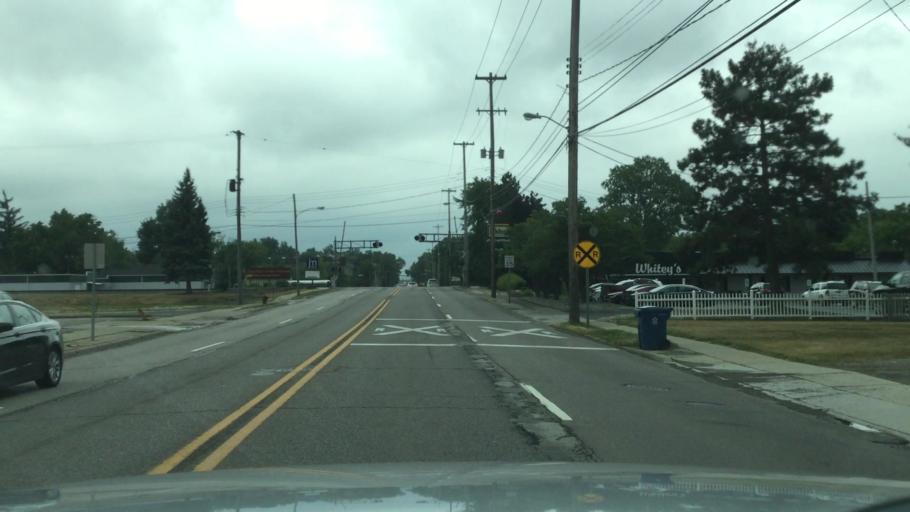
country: US
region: Michigan
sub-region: Genesee County
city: Davison
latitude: 43.0314
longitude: -83.5180
